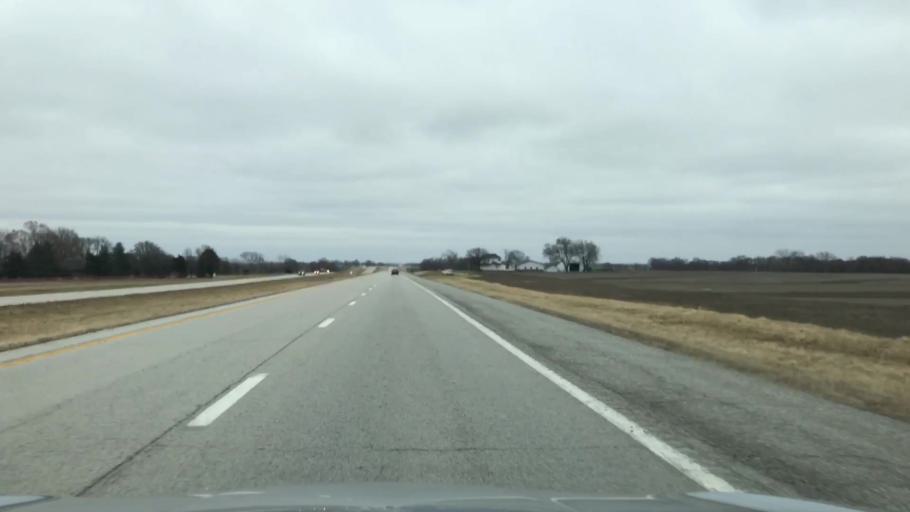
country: US
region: Missouri
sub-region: Livingston County
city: Chillicothe
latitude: 39.7759
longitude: -93.4924
